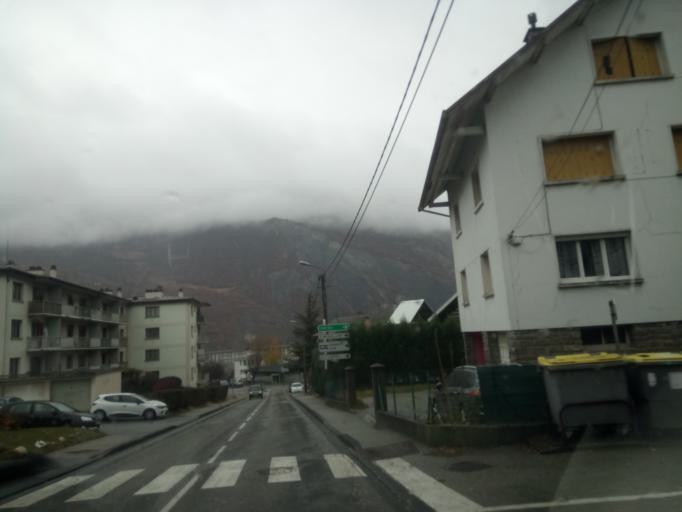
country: FR
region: Rhone-Alpes
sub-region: Departement de la Savoie
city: Saint-Jean-de-Maurienne
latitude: 45.2717
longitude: 6.3492
